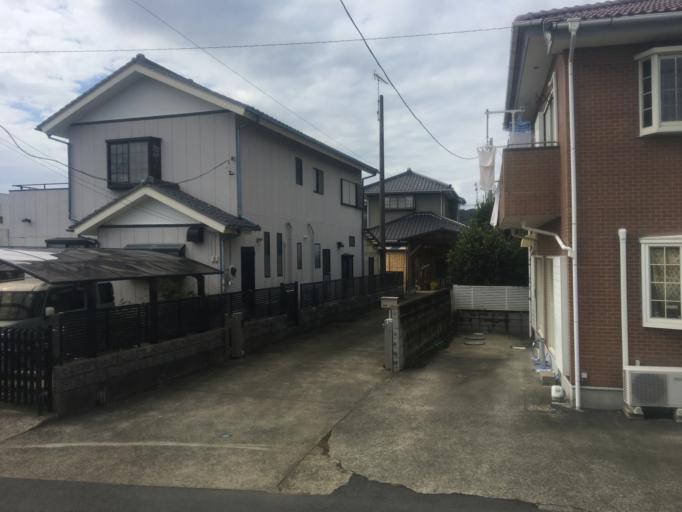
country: JP
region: Chiba
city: Ohara
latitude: 35.2490
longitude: 140.3910
